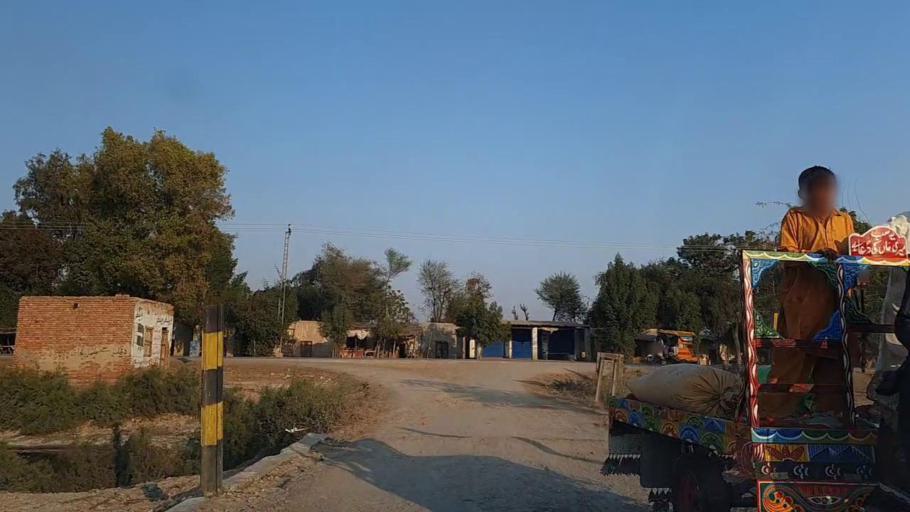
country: PK
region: Sindh
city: Daur
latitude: 26.5104
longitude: 68.3084
